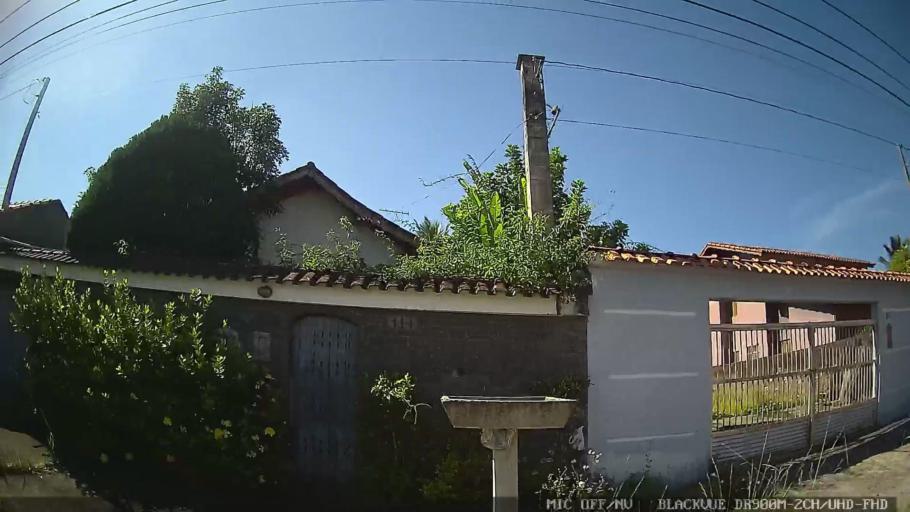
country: BR
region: Sao Paulo
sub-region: Peruibe
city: Peruibe
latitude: -24.2711
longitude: -46.9393
